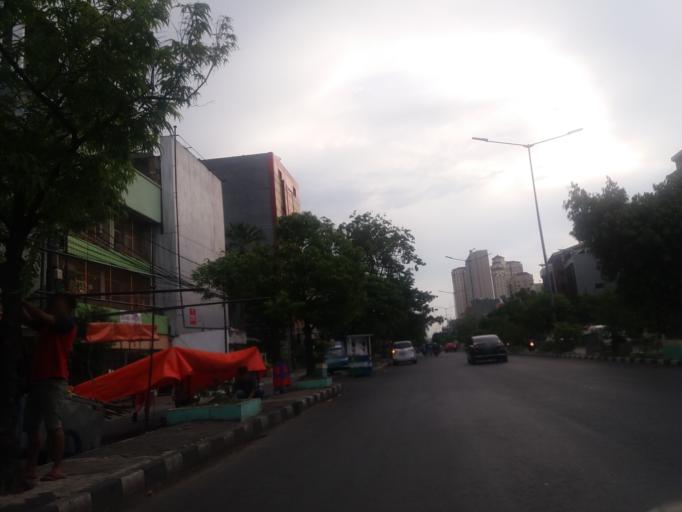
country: ID
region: Jakarta Raya
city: Jakarta
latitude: -6.1492
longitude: 106.8224
